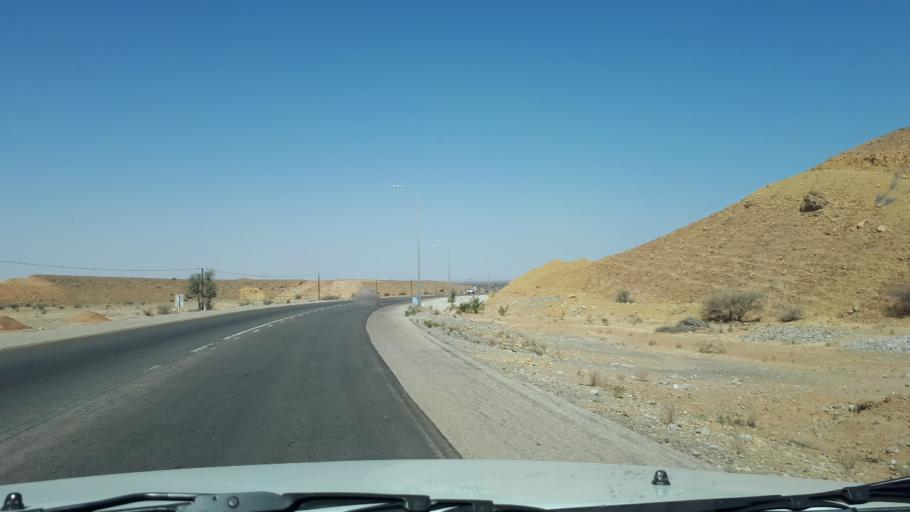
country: OM
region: Ash Sharqiyah
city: Sur
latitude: 22.3153
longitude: 59.3043
